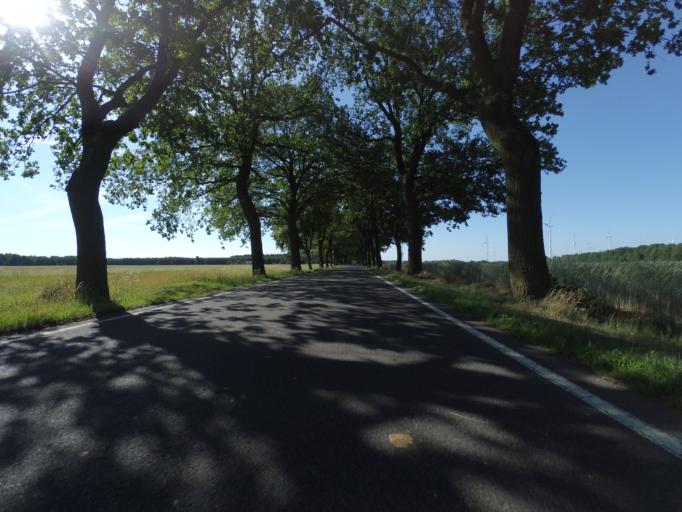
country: DE
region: Brandenburg
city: Putlitz
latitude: 53.3481
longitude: 12.0380
